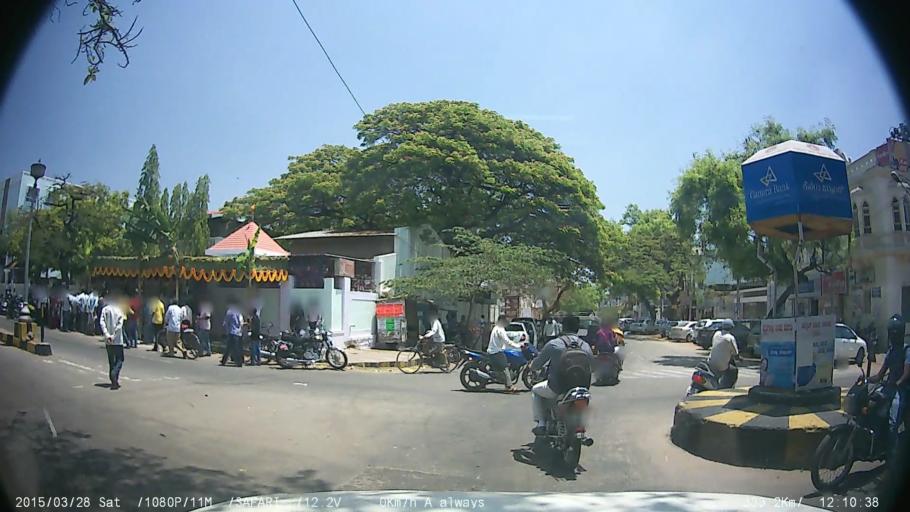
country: IN
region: Karnataka
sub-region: Mysore
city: Mysore
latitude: 12.3059
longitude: 76.6467
